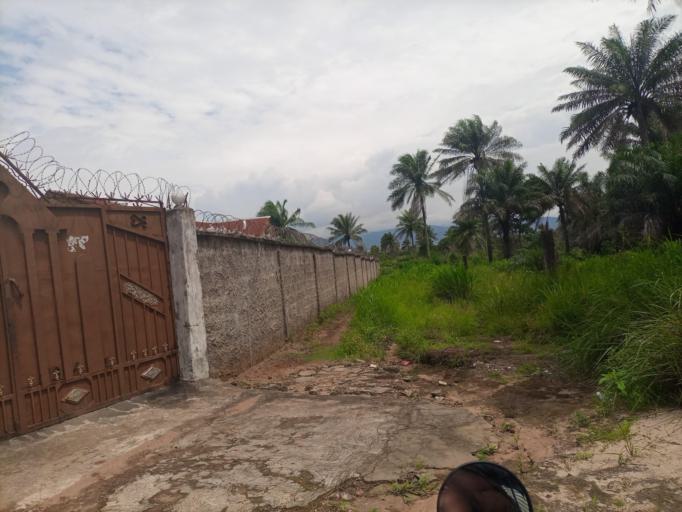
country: SL
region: Northern Province
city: Masoyila
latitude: 8.5453
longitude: -13.1585
